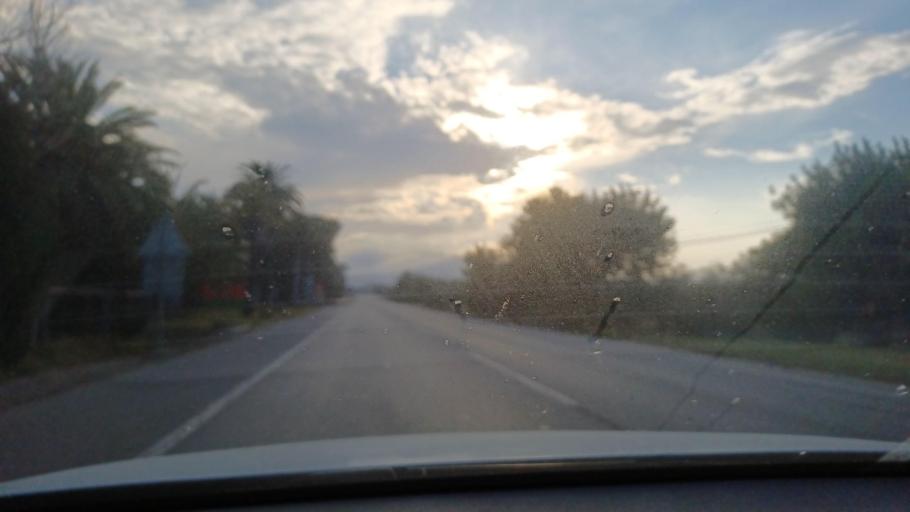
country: ES
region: Catalonia
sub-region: Provincia de Tarragona
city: Cambrils
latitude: 41.0388
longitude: 0.9750
